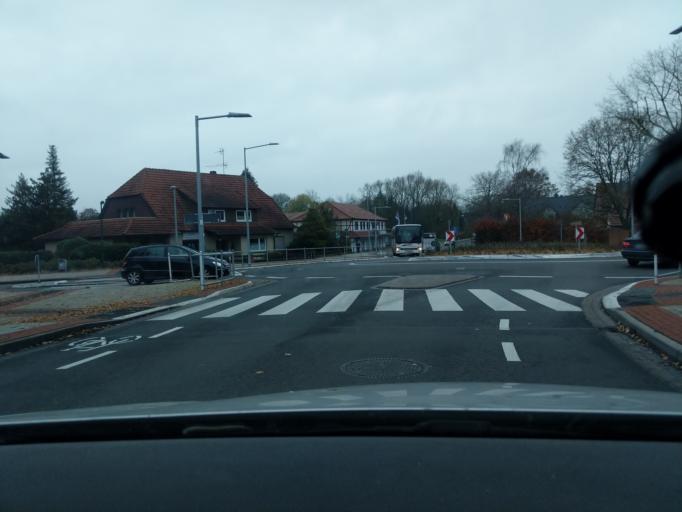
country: DE
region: Lower Saxony
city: Heeslingen
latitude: 53.3151
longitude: 9.3351
